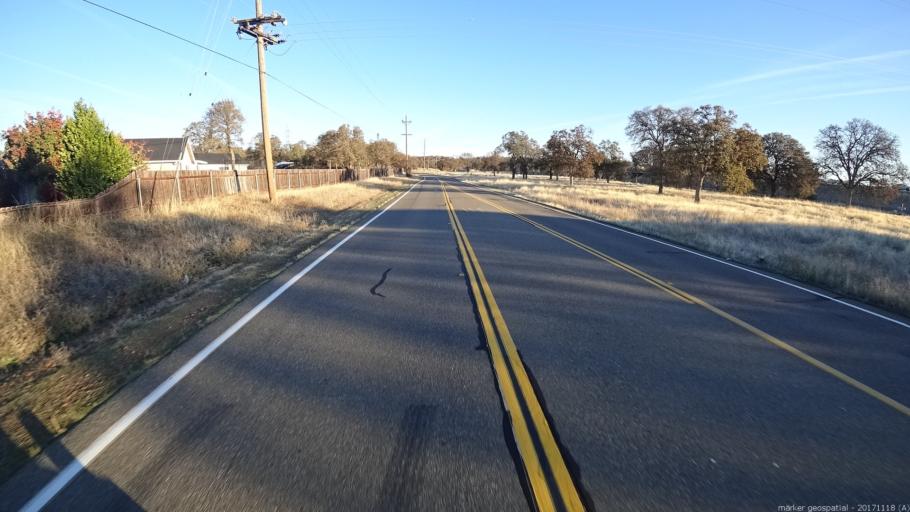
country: US
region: California
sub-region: Shasta County
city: Cottonwood
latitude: 40.4027
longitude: -122.2830
